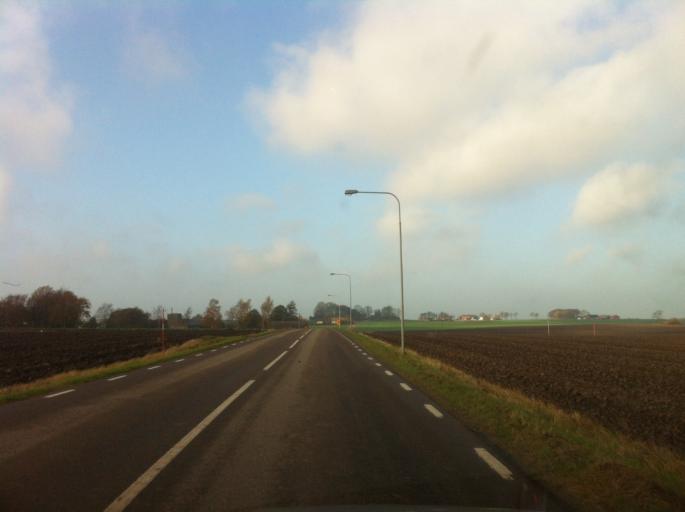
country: SE
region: Skane
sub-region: Helsingborg
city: Glumslov
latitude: 55.9369
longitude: 12.8559
